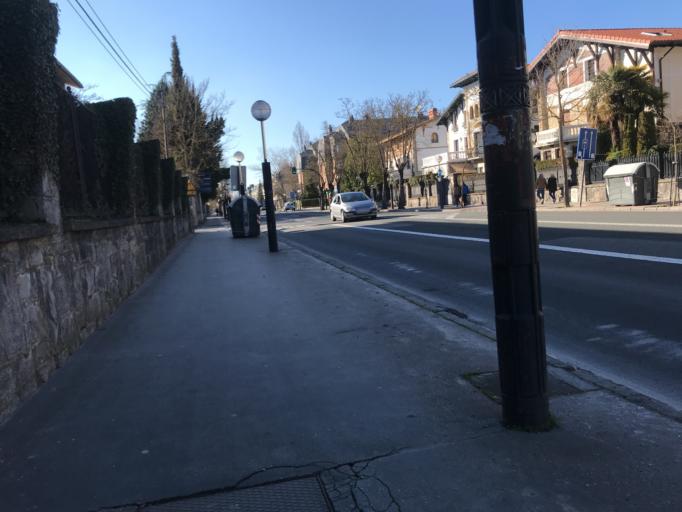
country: ES
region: Basque Country
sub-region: Provincia de Alava
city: Gasteiz / Vitoria
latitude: 42.8372
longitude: -2.6772
